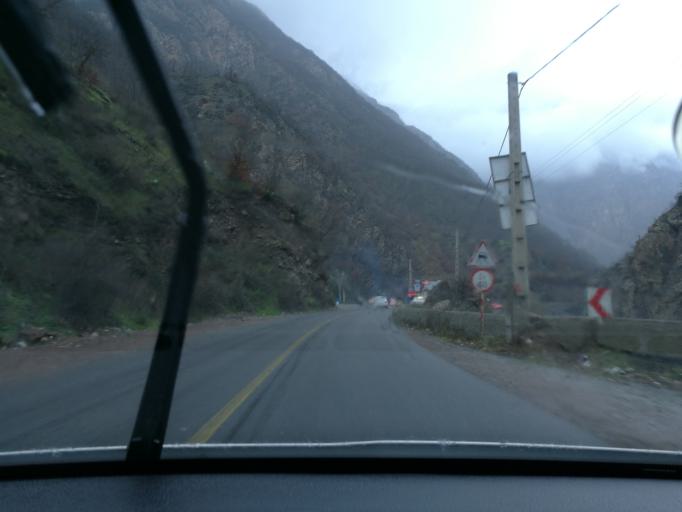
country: IR
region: Mazandaran
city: Chalus
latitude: 36.2646
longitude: 51.2599
